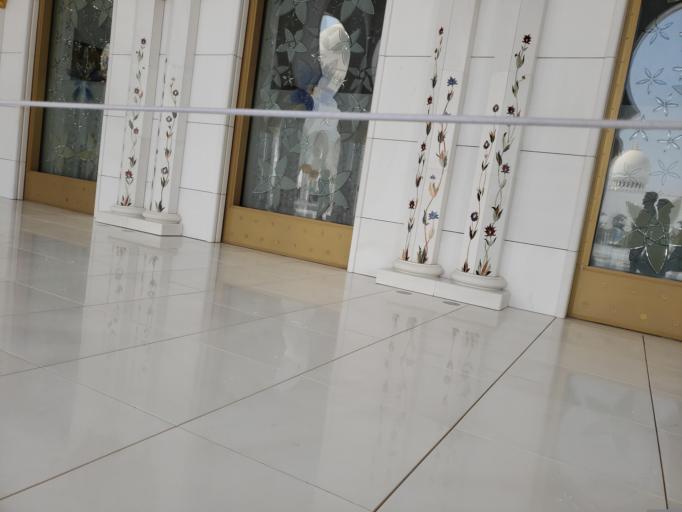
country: AE
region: Abu Dhabi
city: Abu Dhabi
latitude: 24.4121
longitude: 54.4750
